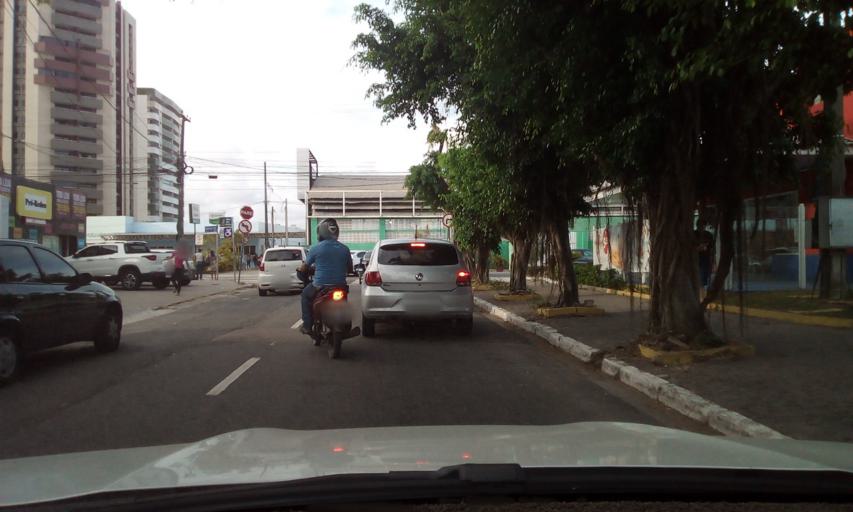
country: BR
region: Paraiba
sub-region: Joao Pessoa
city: Joao Pessoa
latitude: -7.0980
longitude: -34.8395
